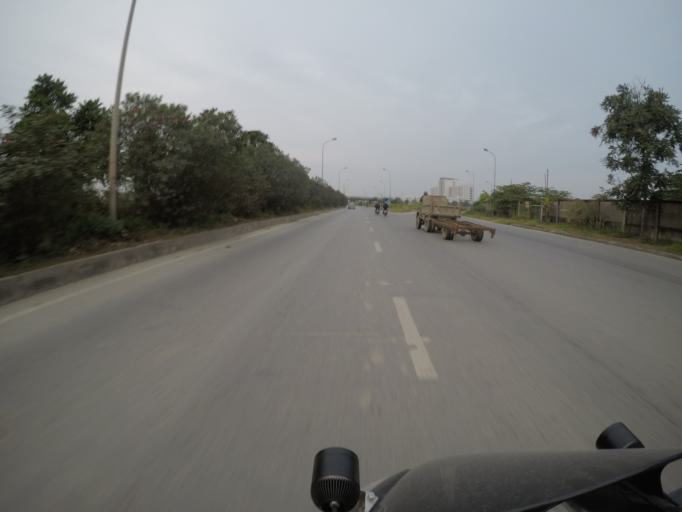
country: VN
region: Ha Noi
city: Cau Dien
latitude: 21.0095
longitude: 105.7502
